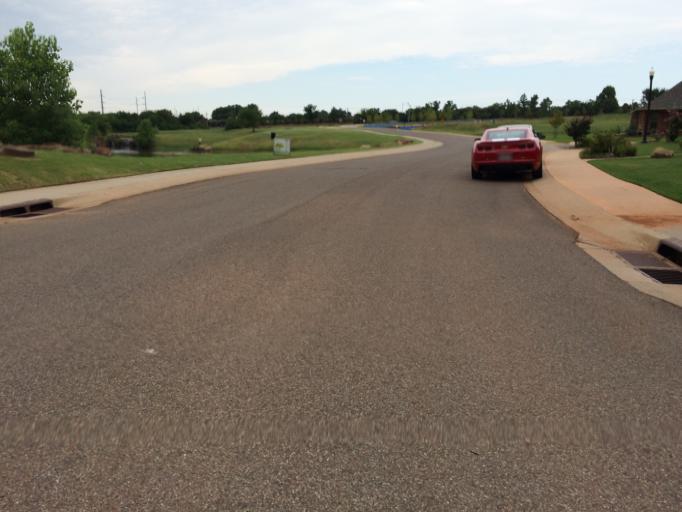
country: US
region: Oklahoma
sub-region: Cleveland County
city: Hall Park
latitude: 35.2451
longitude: -97.4115
